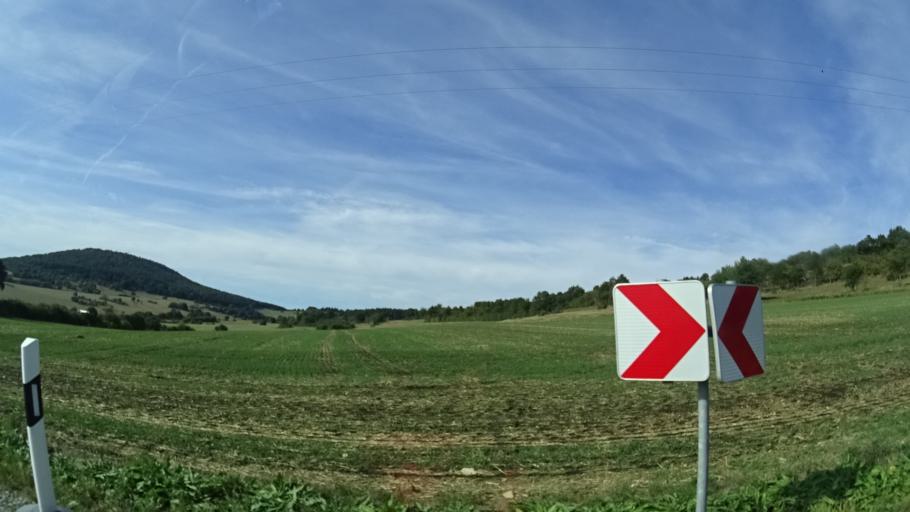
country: DE
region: Thuringia
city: Oberkatz
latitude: 50.5774
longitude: 10.2411
